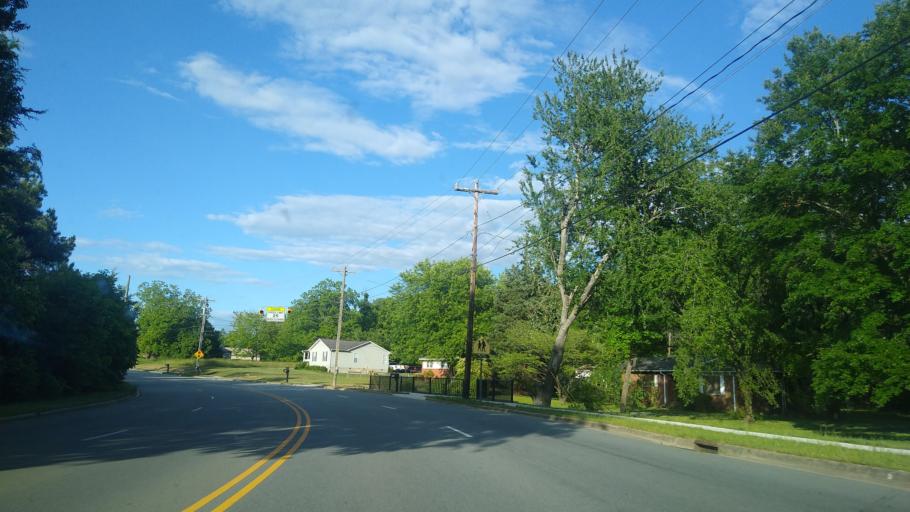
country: US
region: North Carolina
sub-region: Guilford County
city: Greensboro
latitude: 36.1460
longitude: -79.7560
